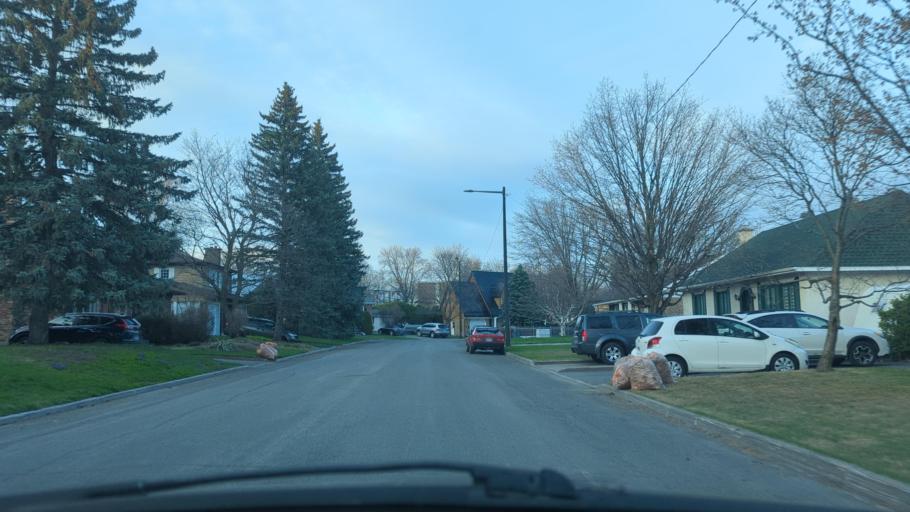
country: CA
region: Quebec
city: Quebec
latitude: 46.8519
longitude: -71.2604
